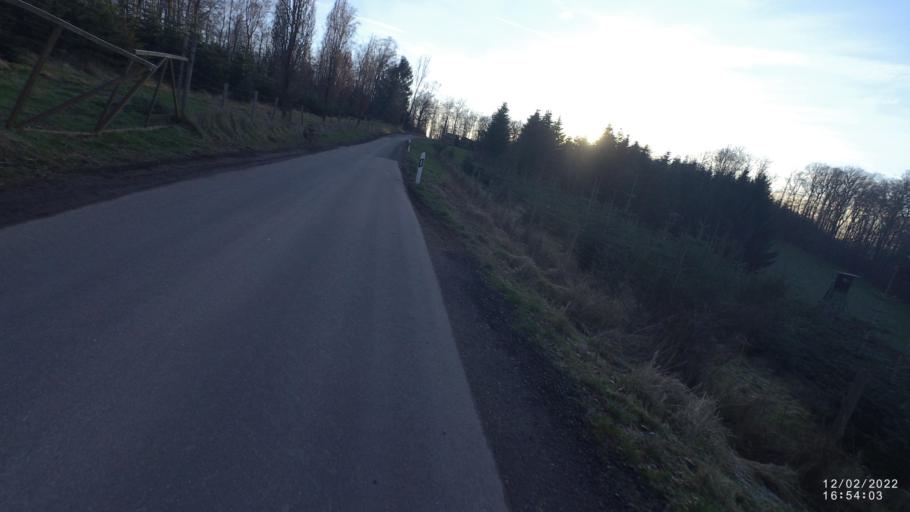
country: DE
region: North Rhine-Westphalia
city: Werdohl
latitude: 51.2718
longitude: 7.7623
